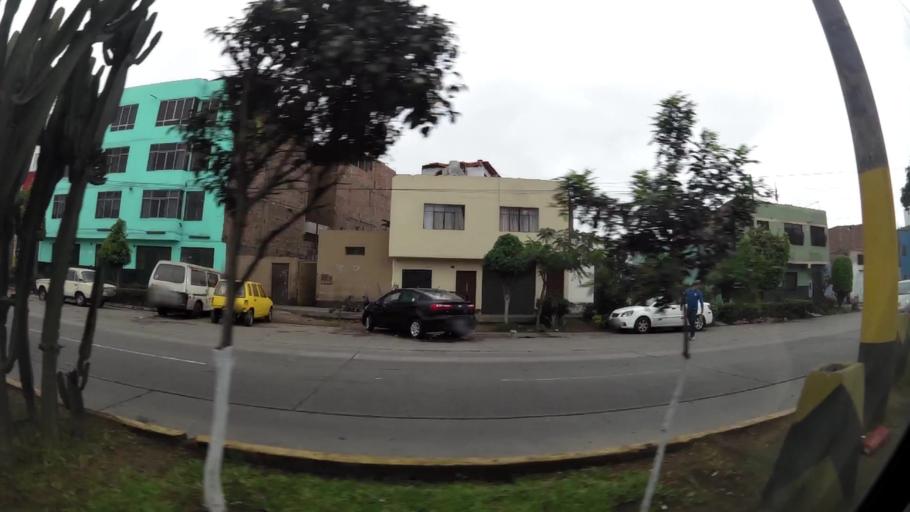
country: PE
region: Lima
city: Lima
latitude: -12.0645
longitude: -77.0533
